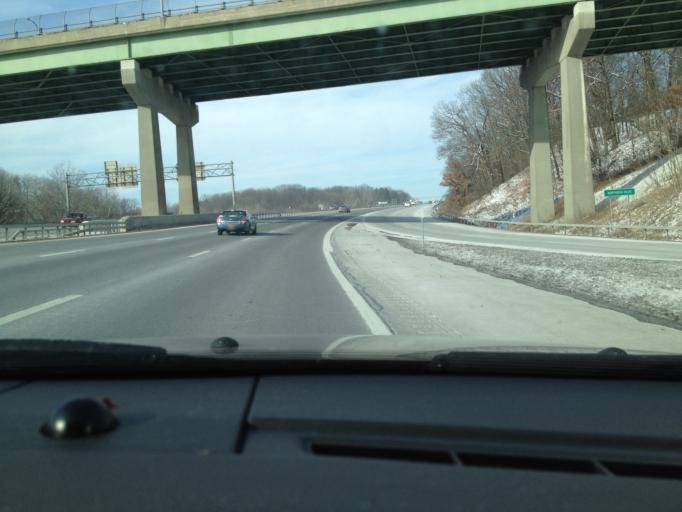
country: US
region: New York
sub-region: Albany County
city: Albany
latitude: 42.6704
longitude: -73.7529
